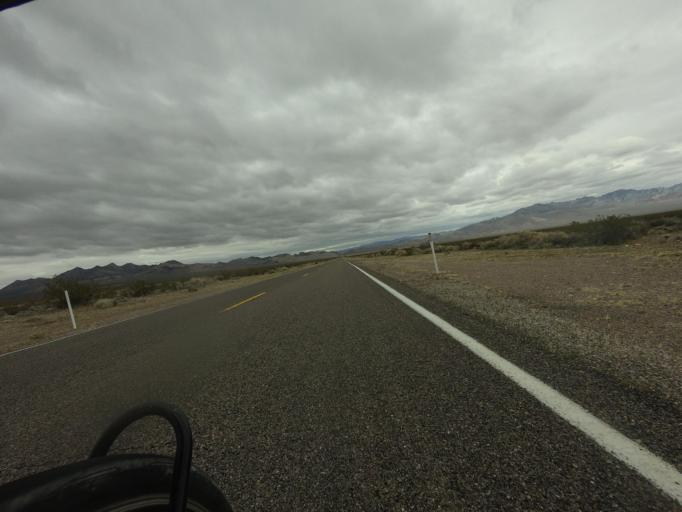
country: US
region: Nevada
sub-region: Nye County
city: Beatty
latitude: 36.8466
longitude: -116.8620
